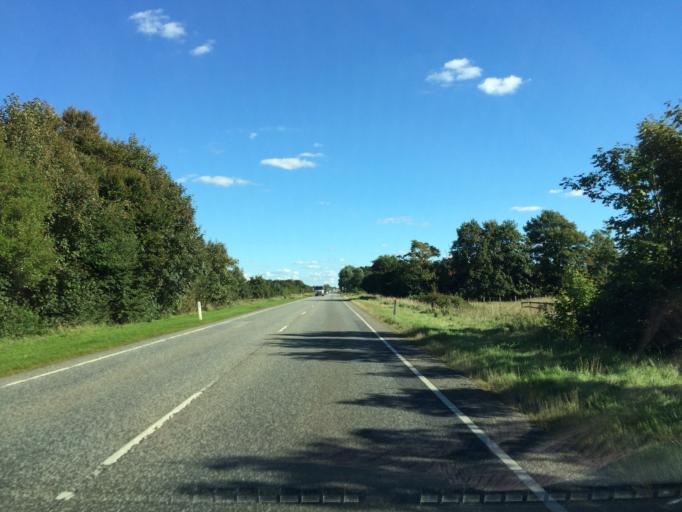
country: DK
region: Central Jutland
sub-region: Holstebro Kommune
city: Holstebro
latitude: 56.3259
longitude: 8.6661
